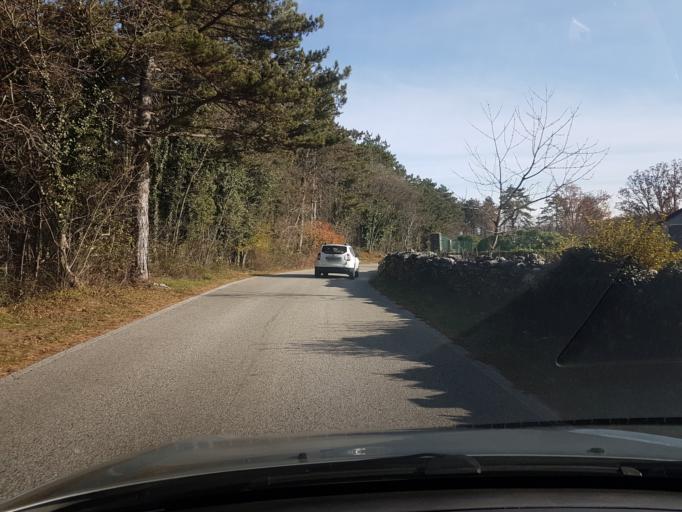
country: IT
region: Friuli Venezia Giulia
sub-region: Provincia di Trieste
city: Aurisina
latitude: 45.7692
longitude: 13.6902
